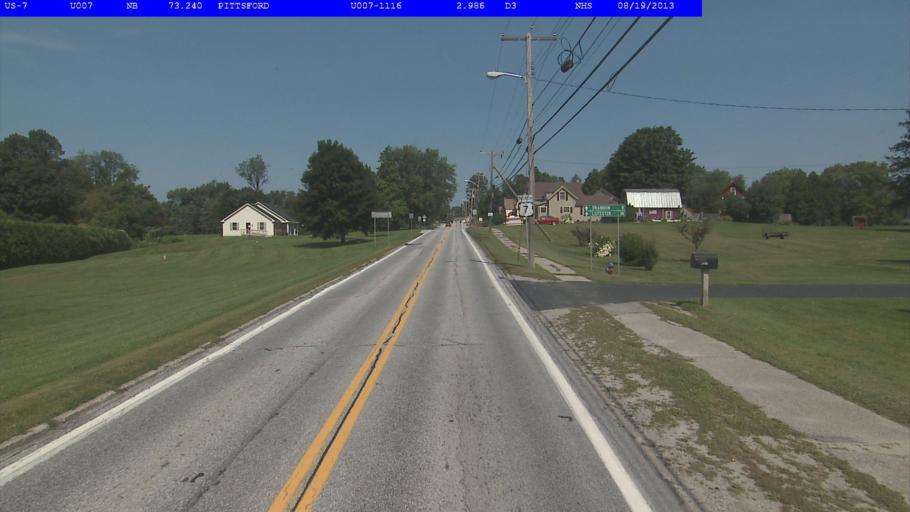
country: US
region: Vermont
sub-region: Rutland County
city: Rutland
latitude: 43.7022
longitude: -73.0119
